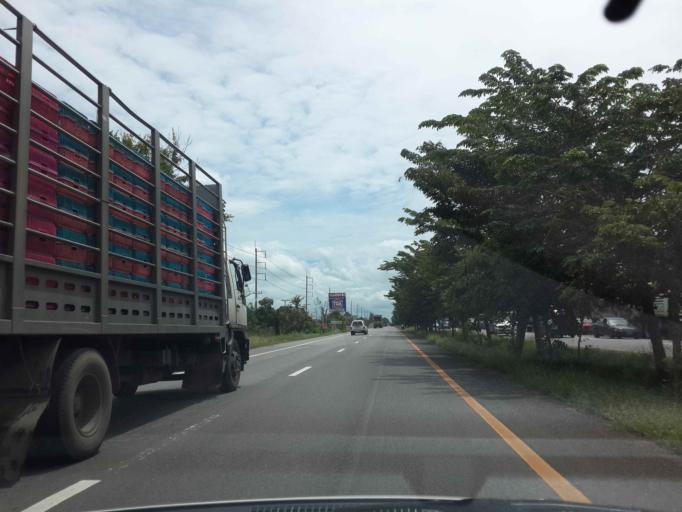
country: TH
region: Ratchaburi
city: Pak Tho
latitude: 13.4073
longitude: 99.8127
